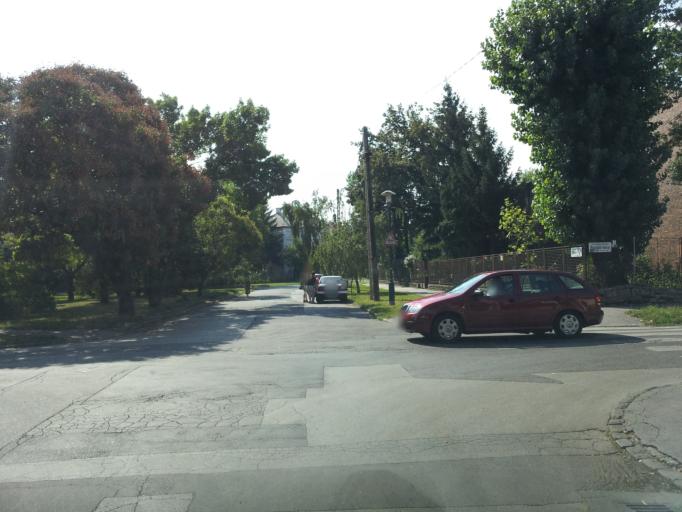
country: HU
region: Budapest
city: Budapest XIV. keruelet
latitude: 47.5118
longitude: 19.1070
